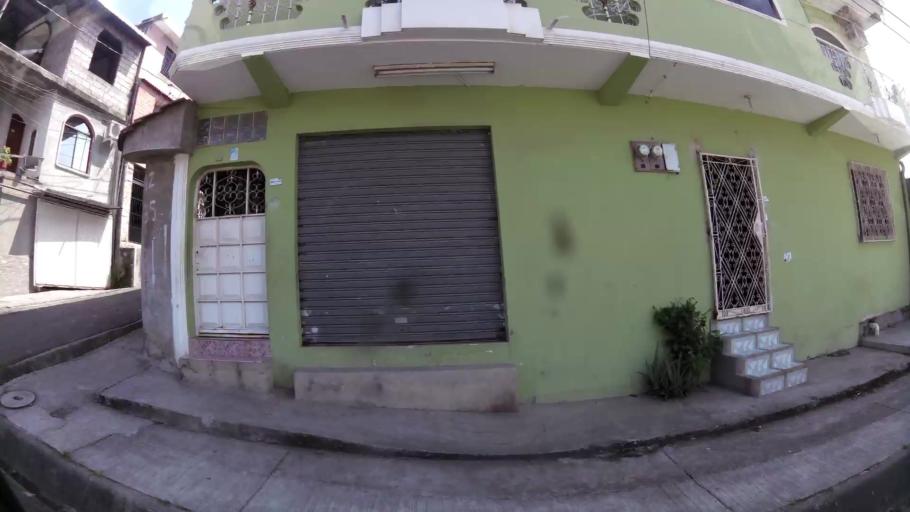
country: EC
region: Guayas
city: Santa Lucia
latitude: -2.1355
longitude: -79.9448
